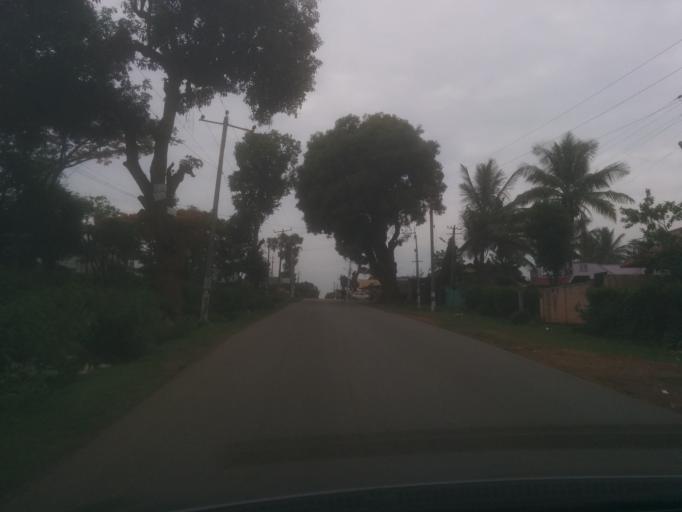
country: IN
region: Karnataka
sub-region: Chikmagalur
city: Chikmagalur
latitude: 13.3455
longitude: 75.7663
